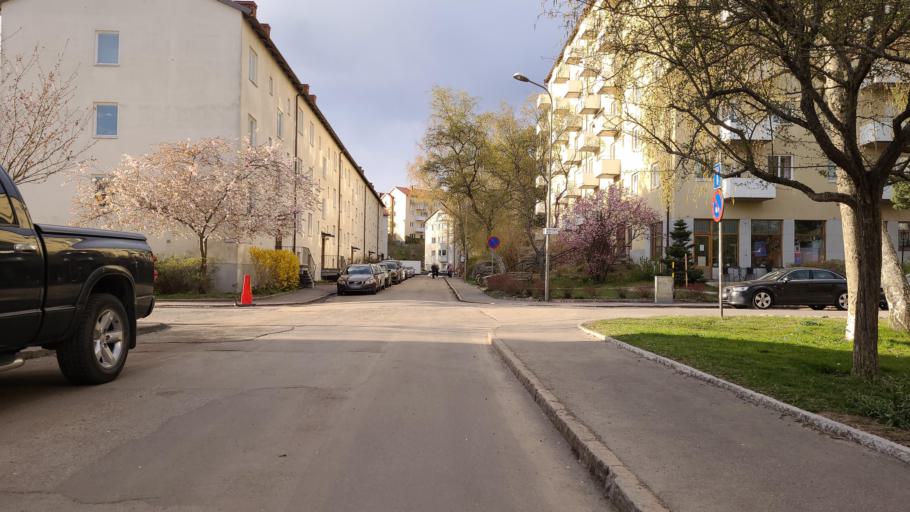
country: SE
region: Stockholm
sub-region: Stockholms Kommun
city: Arsta
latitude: 59.2621
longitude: 18.0805
